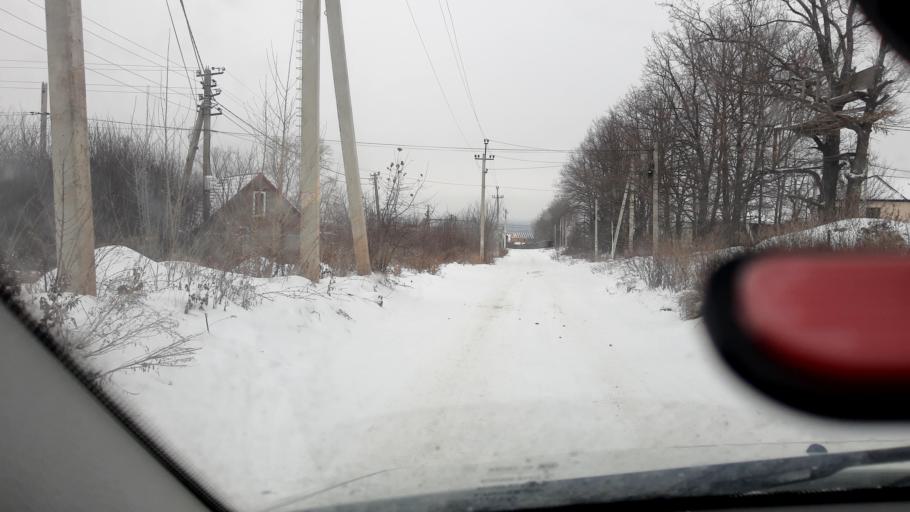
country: RU
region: Bashkortostan
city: Kabakovo
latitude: 54.6312
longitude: 56.0820
